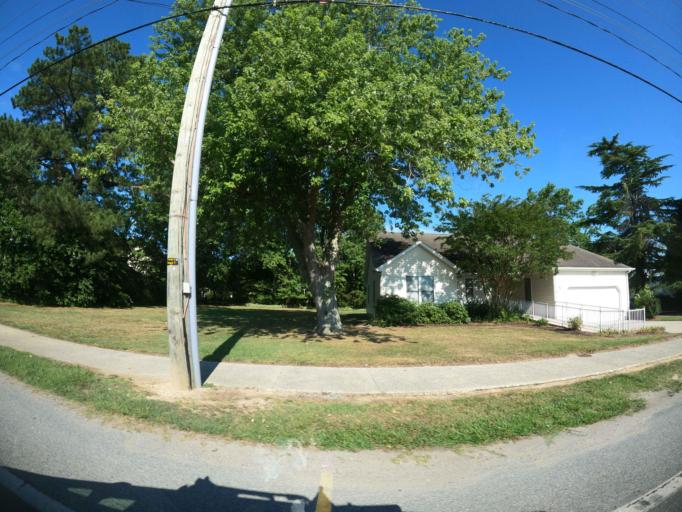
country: US
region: Delaware
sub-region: Sussex County
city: Ocean View
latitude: 38.5425
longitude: -75.0897
